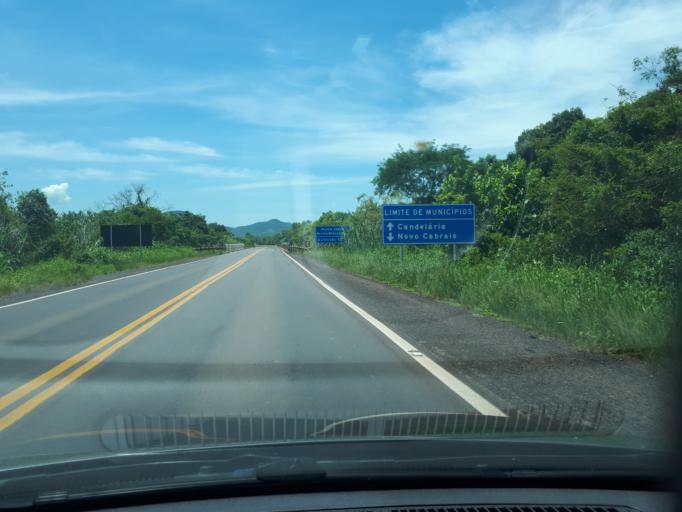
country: BR
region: Rio Grande do Sul
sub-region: Candelaria
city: Candelaria
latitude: -29.7249
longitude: -52.9268
